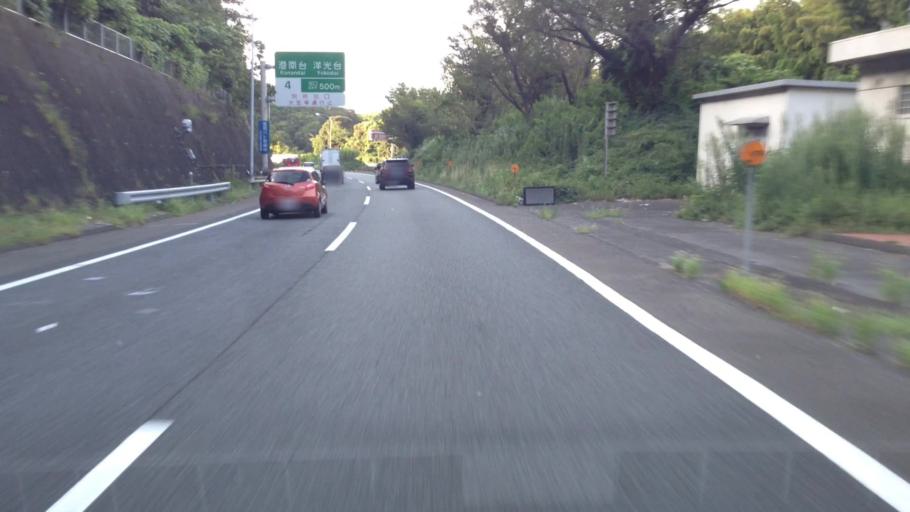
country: JP
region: Kanagawa
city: Kamakura
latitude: 35.3627
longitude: 139.5985
